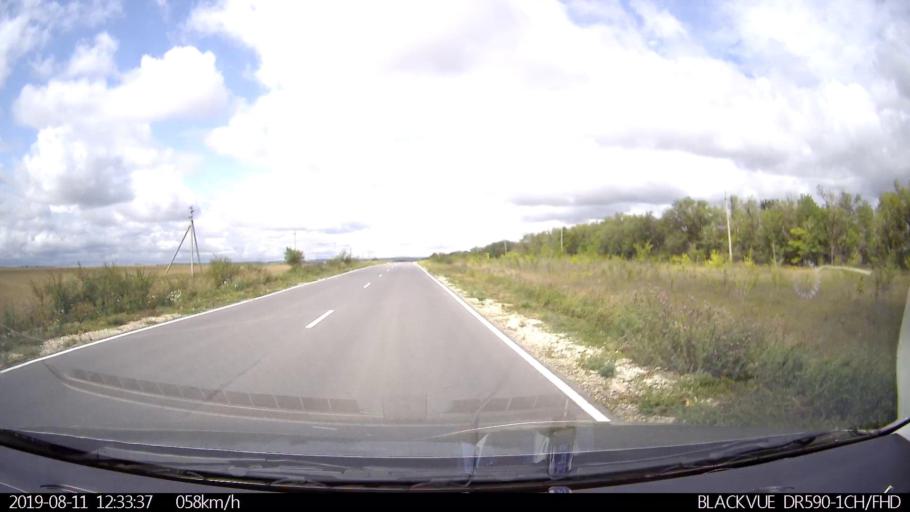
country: RU
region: Ulyanovsk
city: Ignatovka
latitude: 53.8108
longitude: 47.8536
